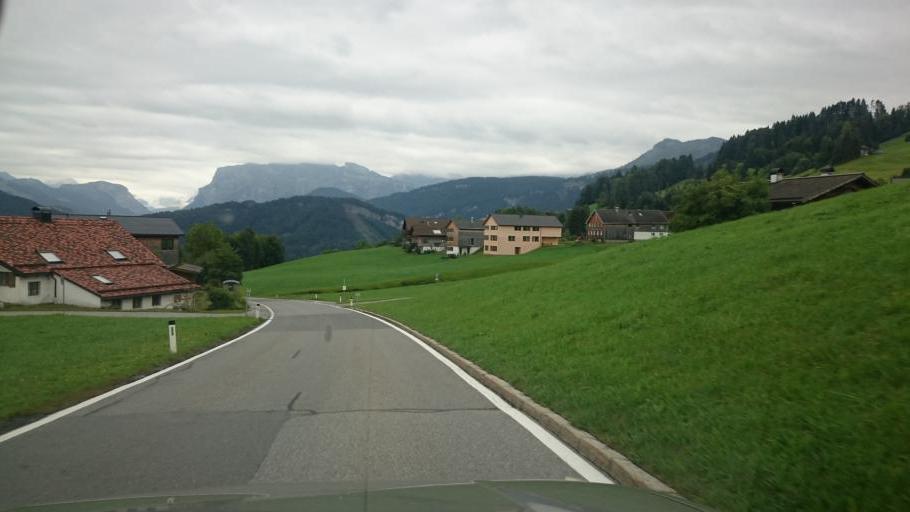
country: AT
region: Vorarlberg
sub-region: Politischer Bezirk Bregenz
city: Andelsbuch
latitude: 47.4177
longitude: 9.8408
